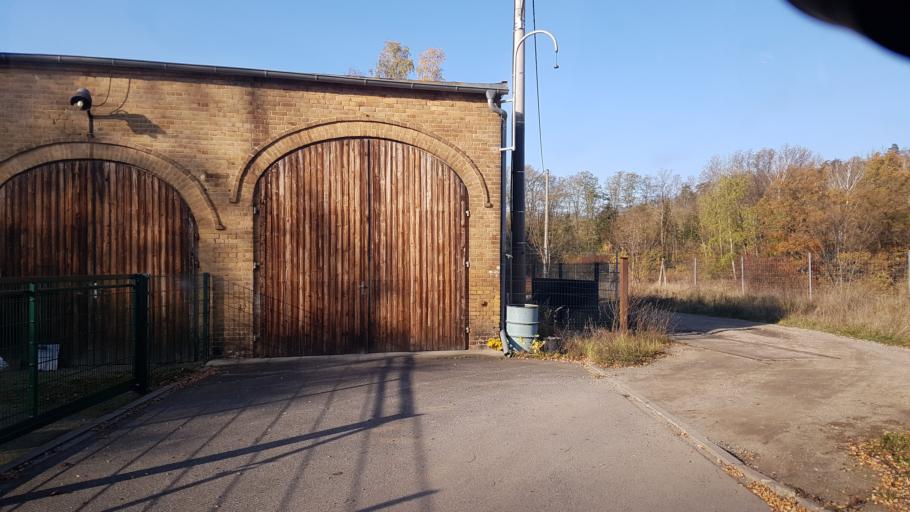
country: DE
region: Brandenburg
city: Sallgast
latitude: 51.5636
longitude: 13.8840
